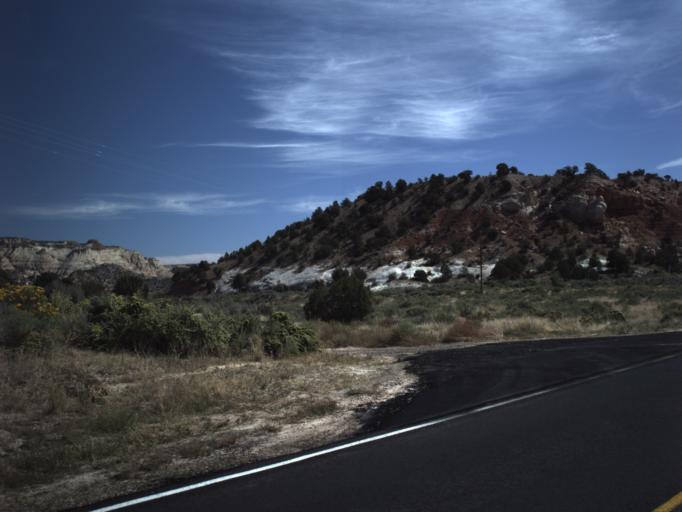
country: US
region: Utah
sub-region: Wayne County
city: Loa
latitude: 37.7768
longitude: -111.6203
